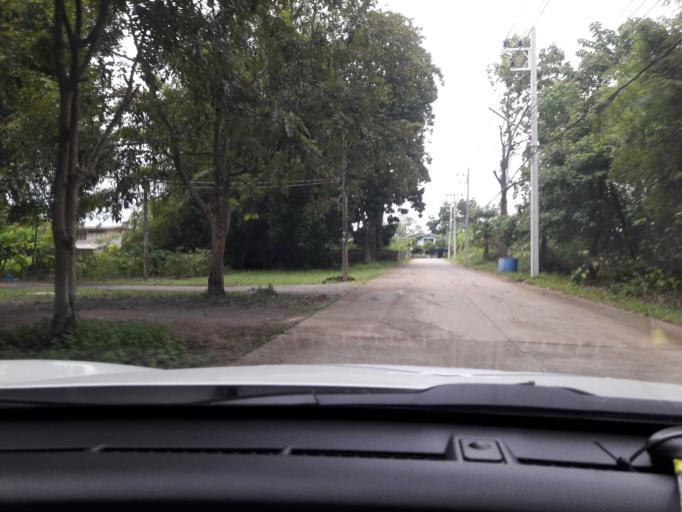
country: TH
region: Nakhon Sawan
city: Tak Fa
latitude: 15.3521
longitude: 100.4945
